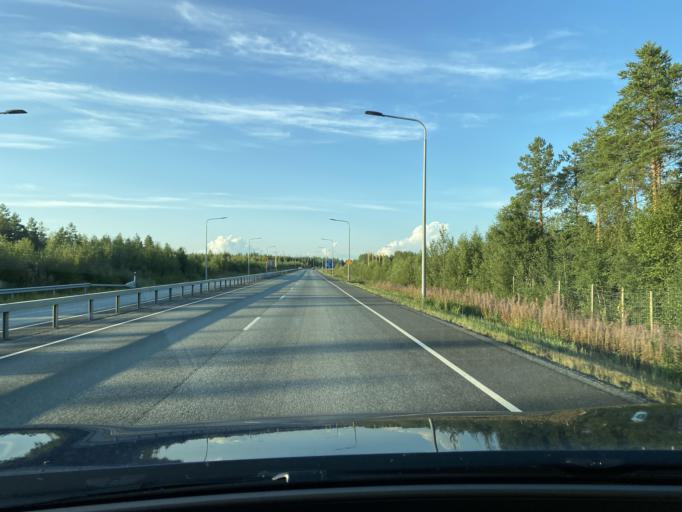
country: FI
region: Southern Ostrobothnia
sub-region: Seinaejoki
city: Seinaejoki
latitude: 62.6969
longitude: 22.8150
